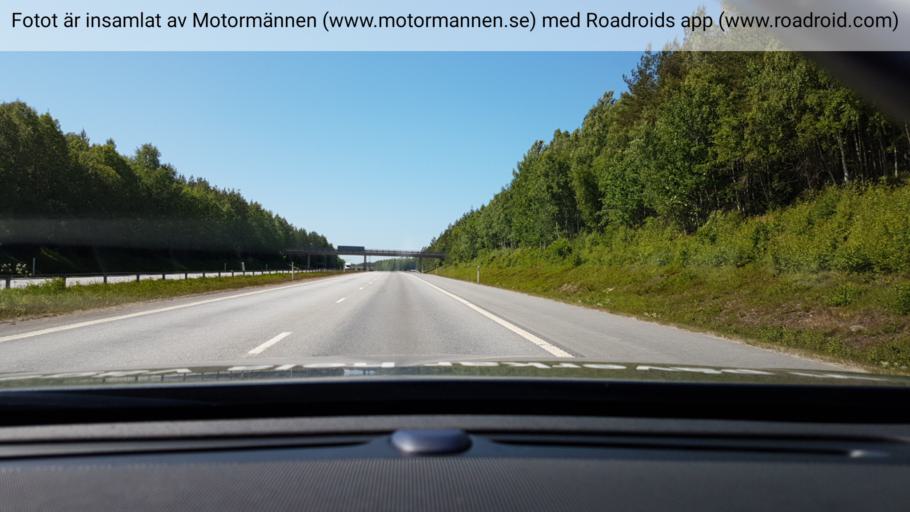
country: SE
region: Vaesterbotten
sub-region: Umea Kommun
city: Roback
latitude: 63.7938
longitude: 20.2173
